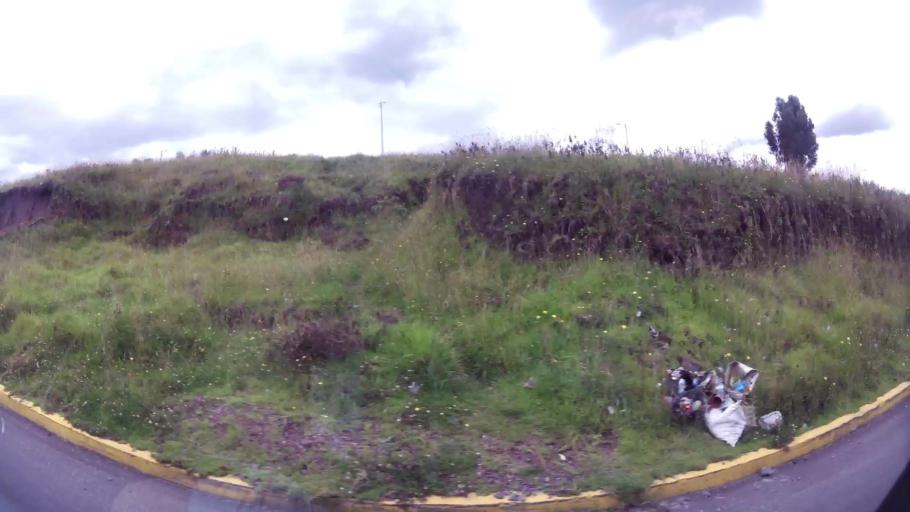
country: EC
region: Pichincha
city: Sangolqui
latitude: -0.3270
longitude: -78.5242
